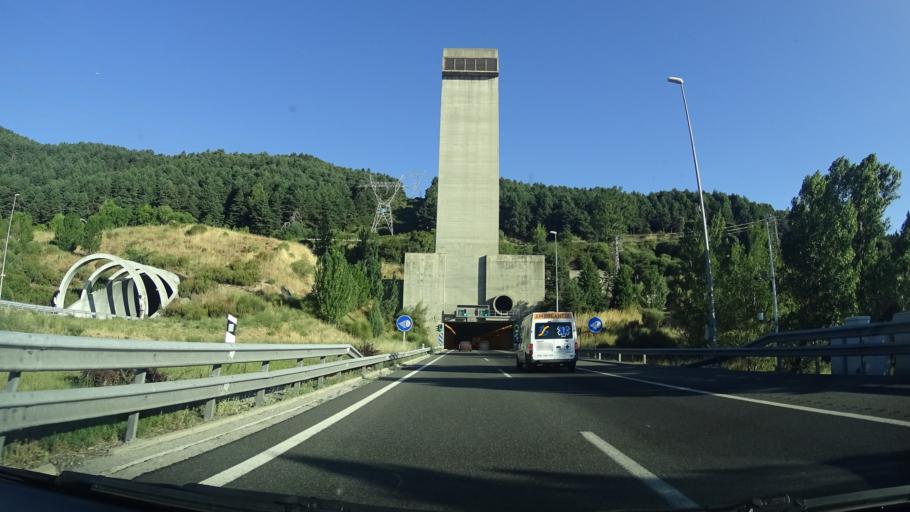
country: ES
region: Madrid
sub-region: Provincia de Madrid
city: Guadarrama
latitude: 40.6995
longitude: -4.1288
